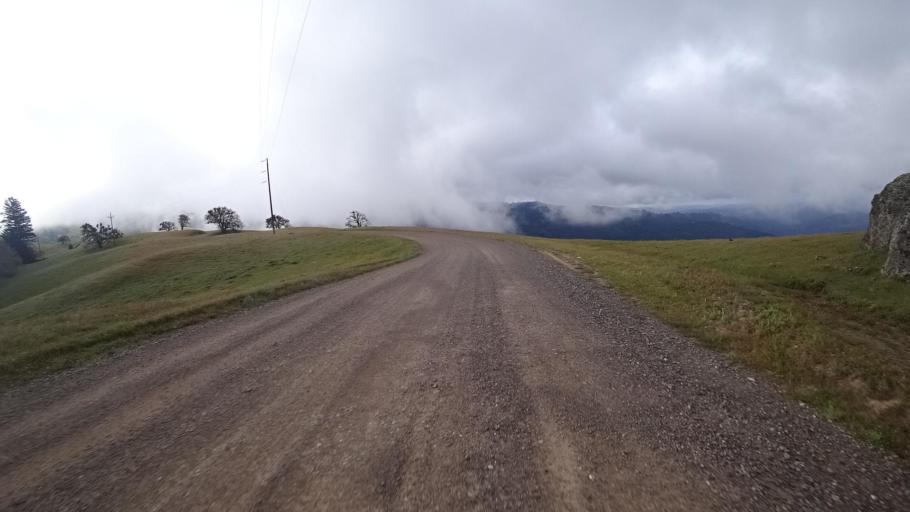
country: US
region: California
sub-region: Humboldt County
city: Redway
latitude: 40.2067
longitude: -123.7291
